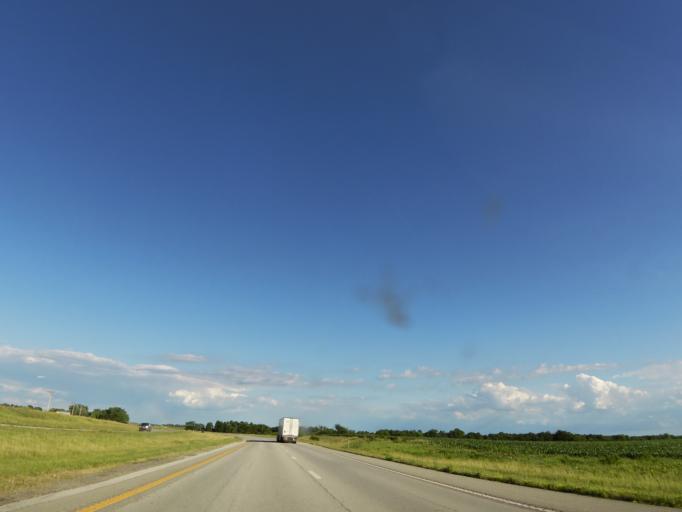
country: US
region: Missouri
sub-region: Pike County
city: Bowling Green
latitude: 39.2786
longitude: -91.0964
